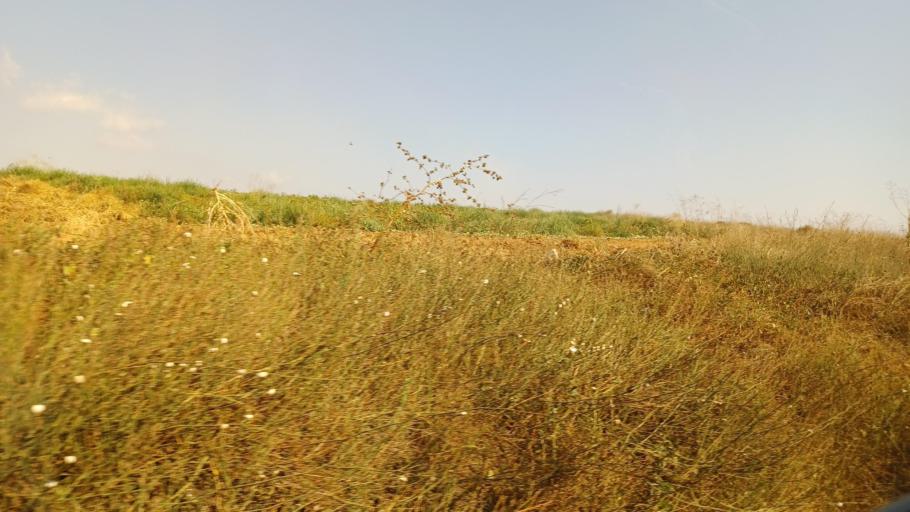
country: CY
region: Ammochostos
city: Paralimni
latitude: 35.0660
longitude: 33.9978
